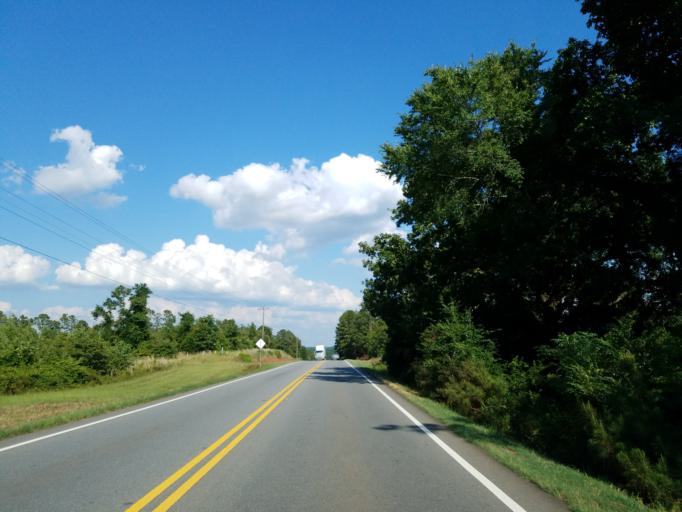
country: US
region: Georgia
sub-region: Peach County
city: Byron
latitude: 32.5528
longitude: -83.7772
